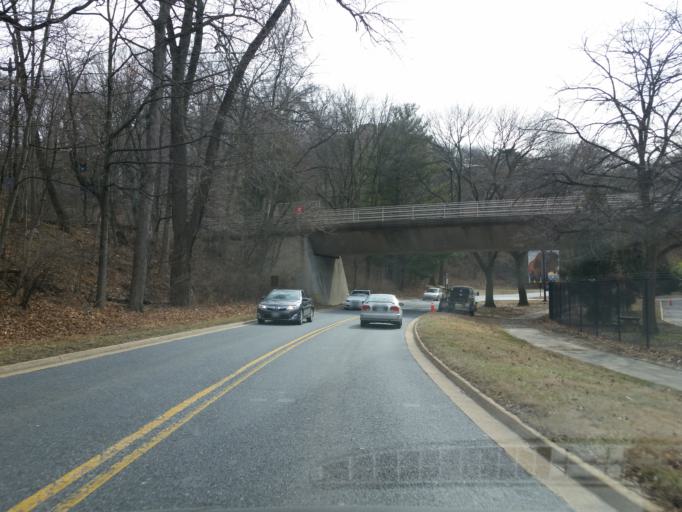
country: US
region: Washington, D.C.
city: Washington, D.C.
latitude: 38.9285
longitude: -77.0439
